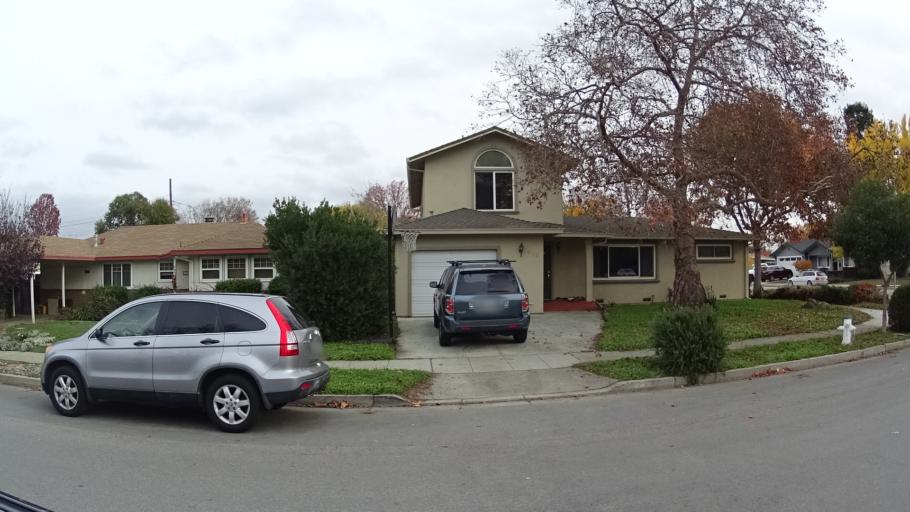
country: US
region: California
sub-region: Santa Clara County
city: Sunnyvale
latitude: 37.3683
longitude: -122.0538
